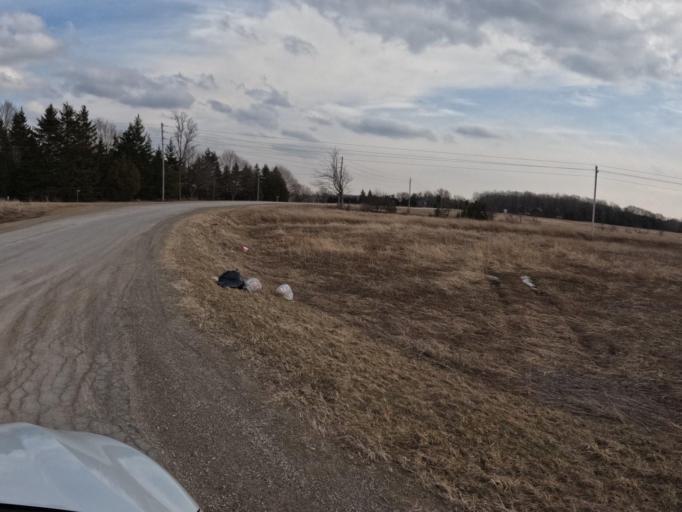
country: CA
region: Ontario
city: Shelburne
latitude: 43.9268
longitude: -80.3079
